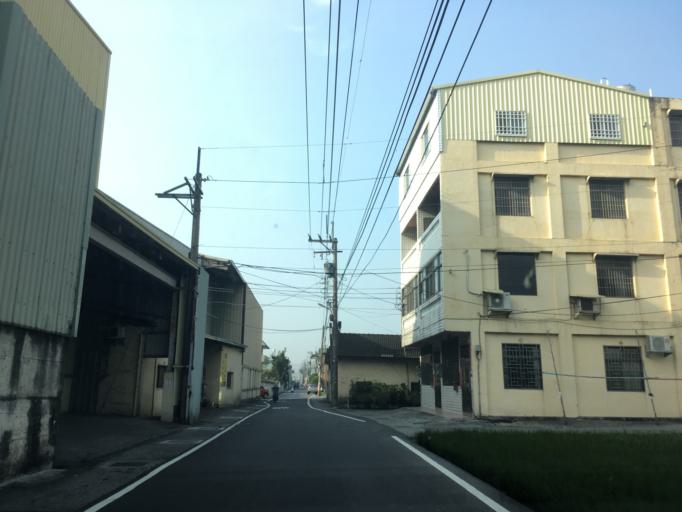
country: TW
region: Taiwan
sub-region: Taichung City
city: Taichung
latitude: 24.0663
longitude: 120.6799
